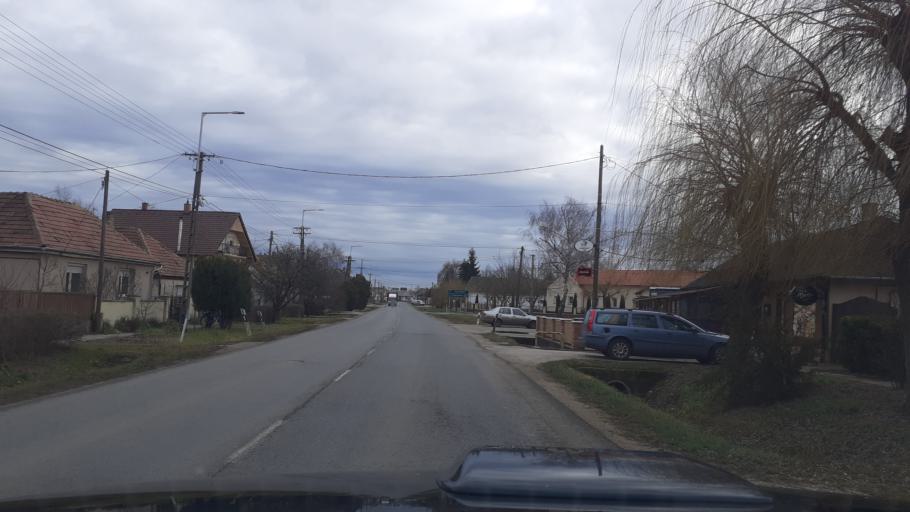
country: HU
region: Fejer
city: Seregelyes
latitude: 47.1117
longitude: 18.5781
